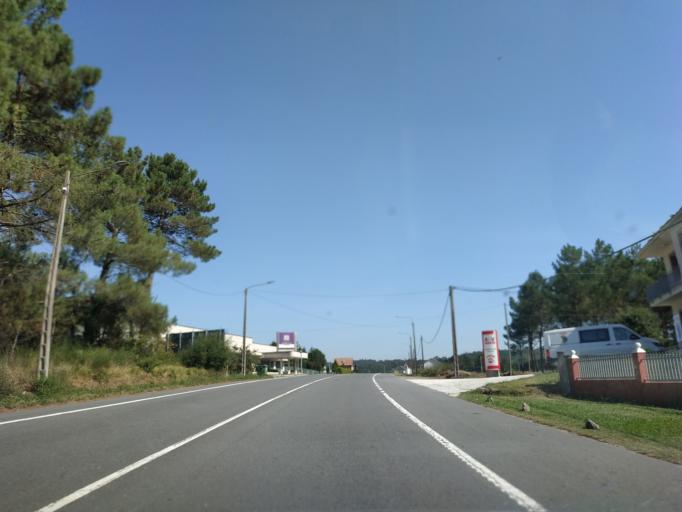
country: ES
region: Galicia
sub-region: Provincia da Coruna
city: Carballo
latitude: 43.2305
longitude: -8.6606
